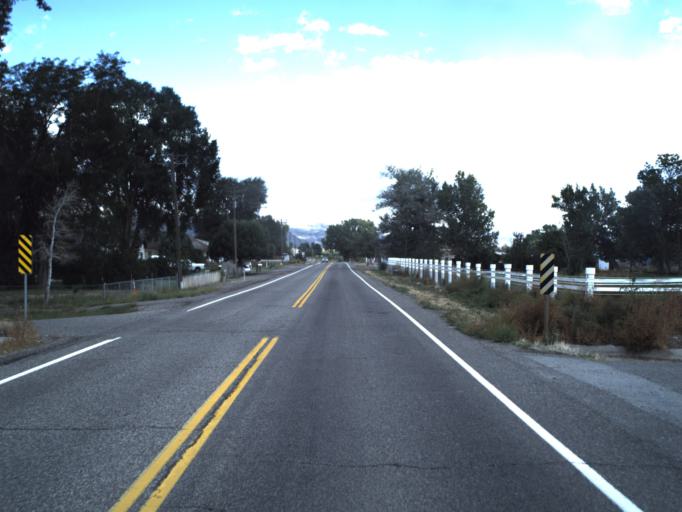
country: US
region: Utah
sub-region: Sevier County
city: Monroe
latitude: 38.6713
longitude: -112.1209
